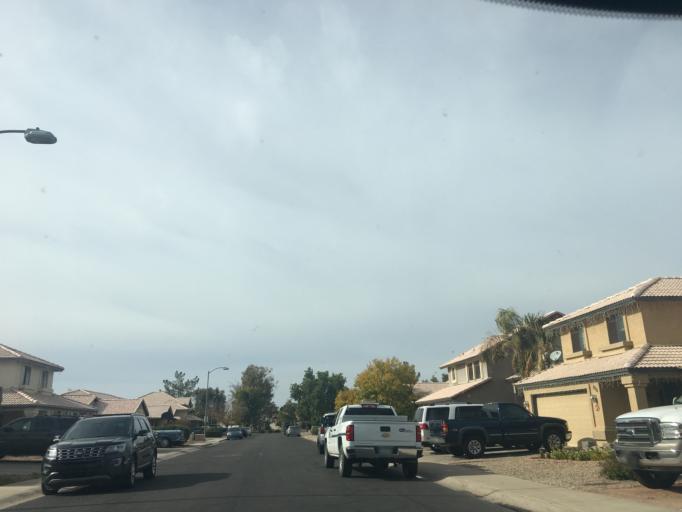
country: US
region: Arizona
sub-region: Maricopa County
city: Gilbert
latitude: 33.3471
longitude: -111.8016
